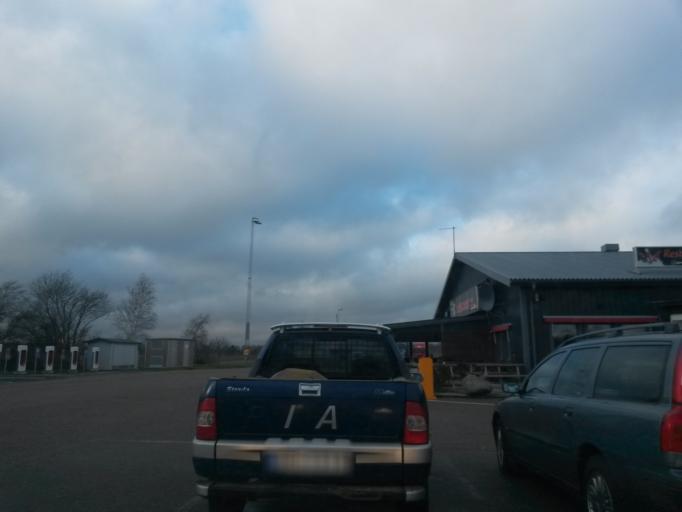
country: SE
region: Vaestra Goetaland
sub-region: Vara Kommun
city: Kvanum
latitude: 58.3276
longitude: 13.1329
